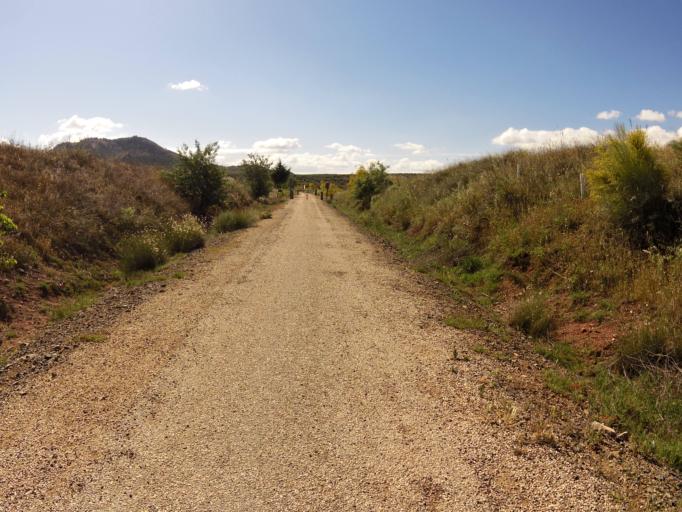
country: ES
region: Andalusia
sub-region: Provincia de Jaen
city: Alcaudete
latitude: 37.6022
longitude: -4.1438
